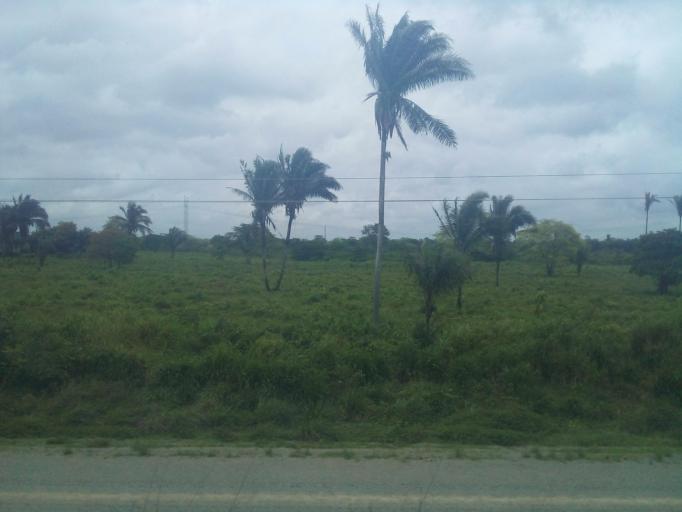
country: BR
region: Maranhao
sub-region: Arari
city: Arari
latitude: -3.5715
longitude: -44.7719
